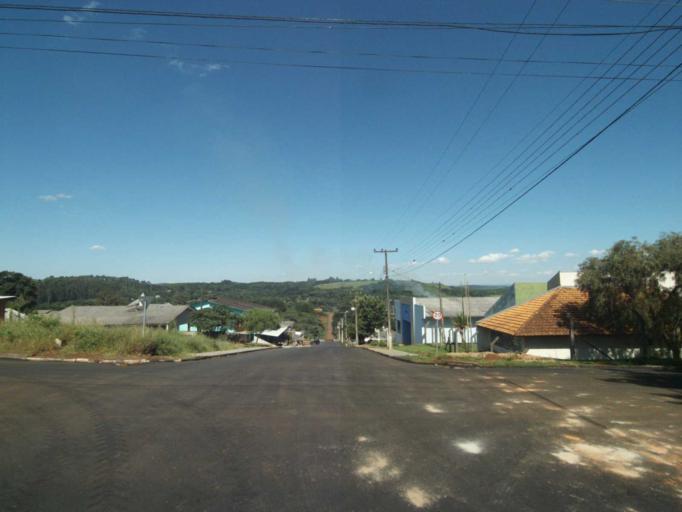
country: BR
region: Parana
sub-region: Laranjeiras Do Sul
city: Laranjeiras do Sul
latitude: -25.3841
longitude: -52.2056
